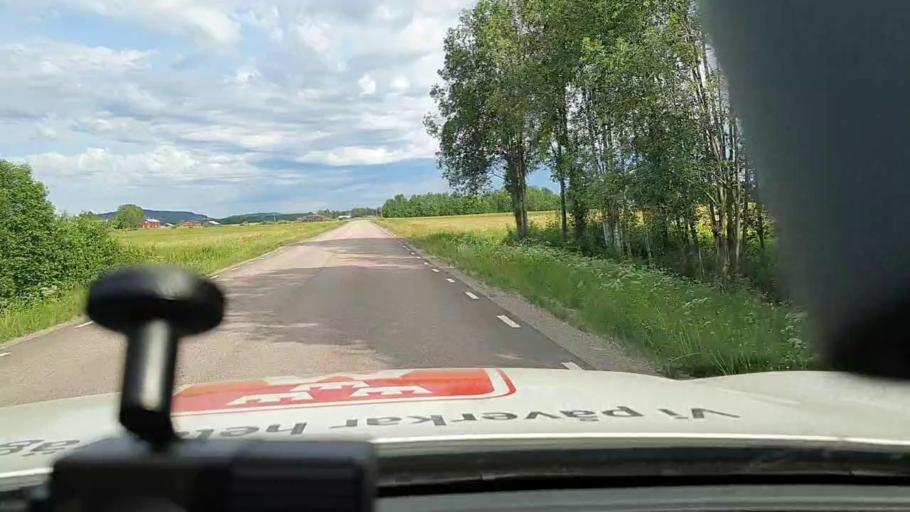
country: SE
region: Norrbotten
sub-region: Bodens Kommun
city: Saevast
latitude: 65.6973
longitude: 21.7763
